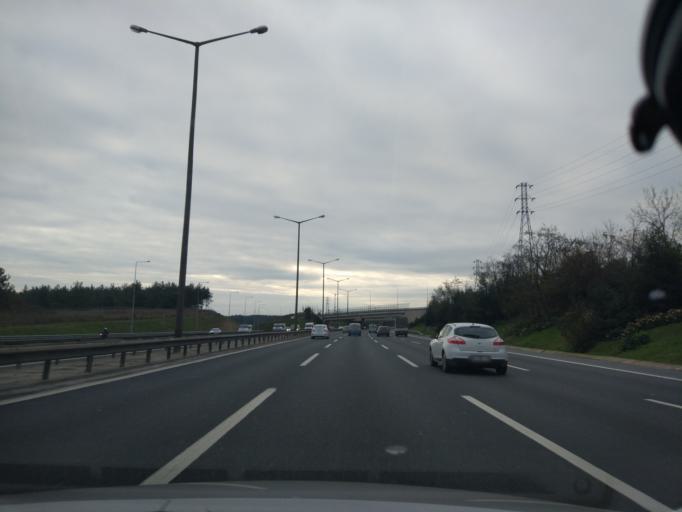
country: TR
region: Istanbul
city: Umraniye
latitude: 41.0564
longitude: 29.1190
